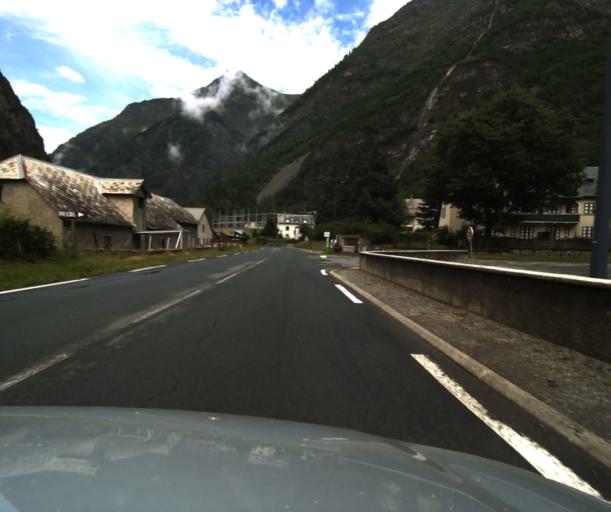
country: FR
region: Midi-Pyrenees
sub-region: Departement des Hautes-Pyrenees
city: Luz-Saint-Sauveur
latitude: 42.8182
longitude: 0.0098
